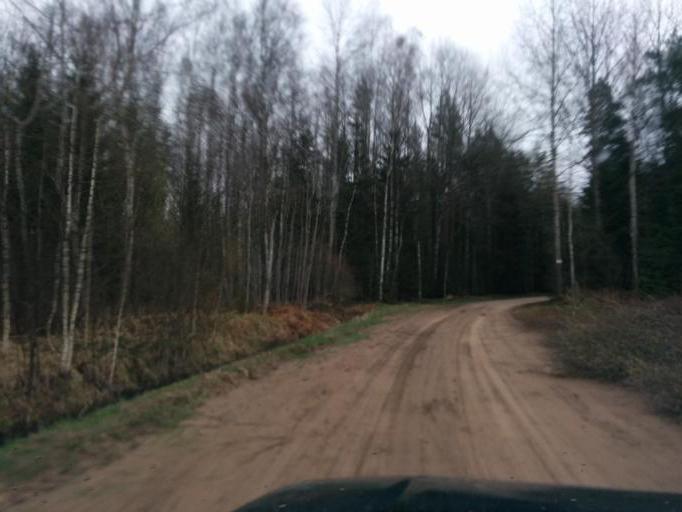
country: LV
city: Tireli
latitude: 56.7983
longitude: 23.6707
